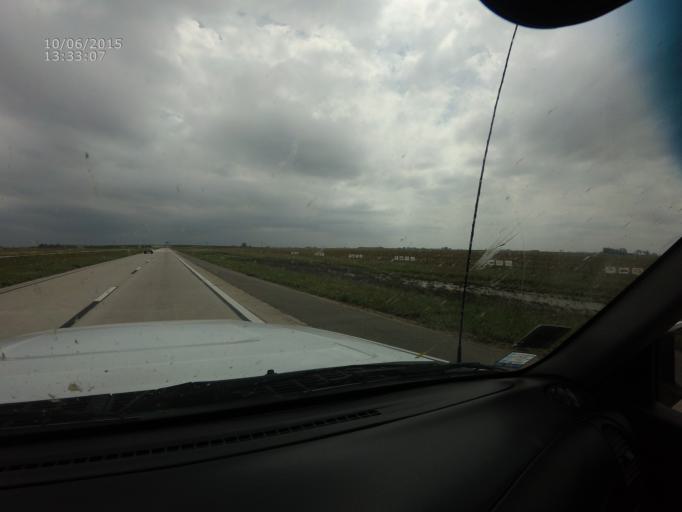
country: AR
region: Cordoba
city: Leones
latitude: -32.6244
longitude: -62.3214
